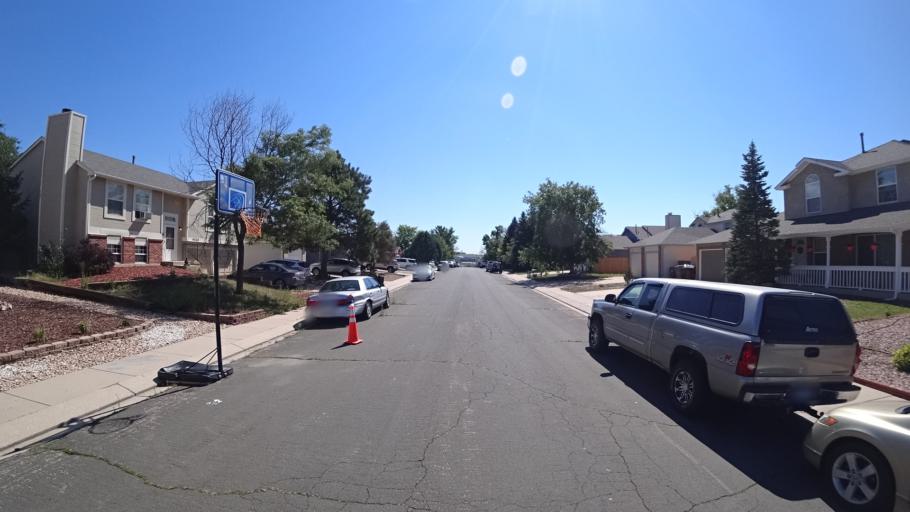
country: US
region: Colorado
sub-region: El Paso County
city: Black Forest
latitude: 38.9415
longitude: -104.7464
